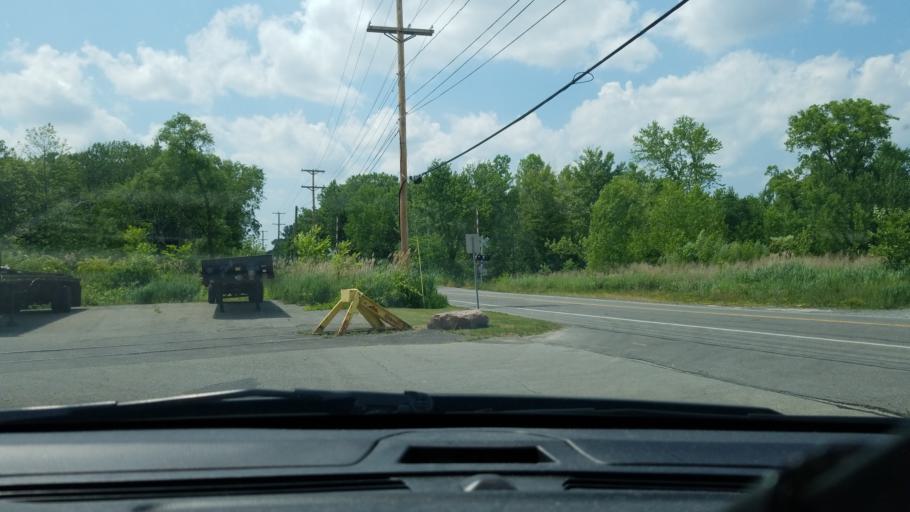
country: US
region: New York
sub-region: Onondaga County
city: Liverpool
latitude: 43.1507
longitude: -76.2023
